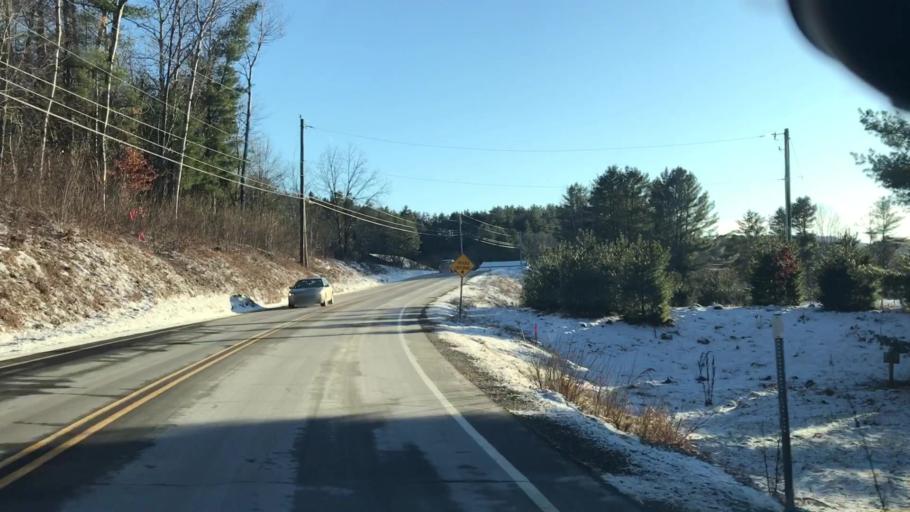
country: US
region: New Hampshire
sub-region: Grafton County
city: Orford
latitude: 43.9235
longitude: -72.1134
